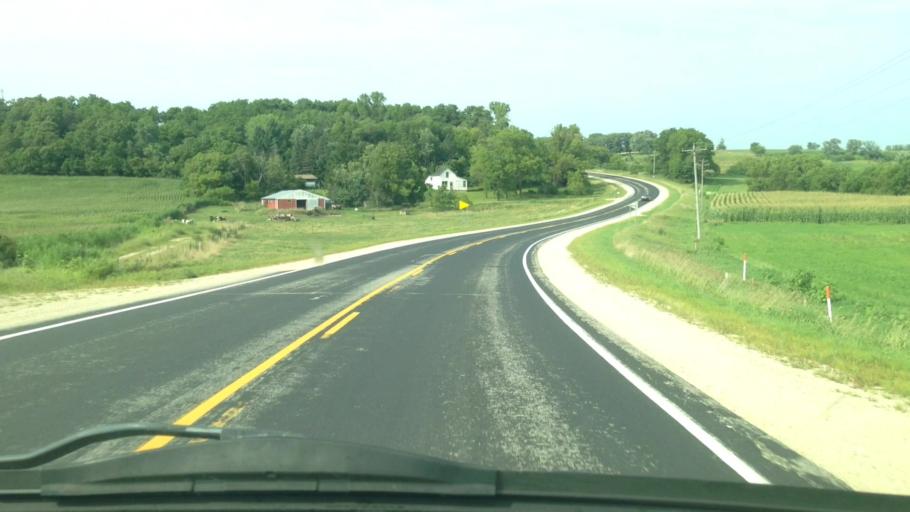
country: US
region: Minnesota
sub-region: Winona County
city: Lewiston
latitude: 43.9224
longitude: -91.9593
